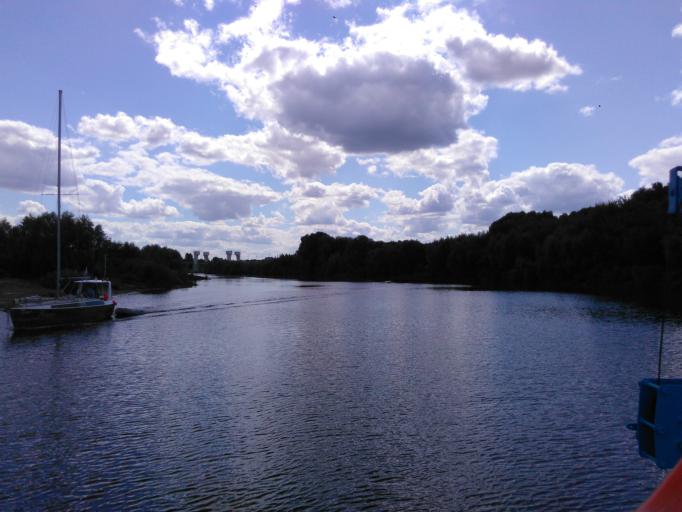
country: RU
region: Rjazan
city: Ryazan'
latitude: 54.6506
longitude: 39.7658
